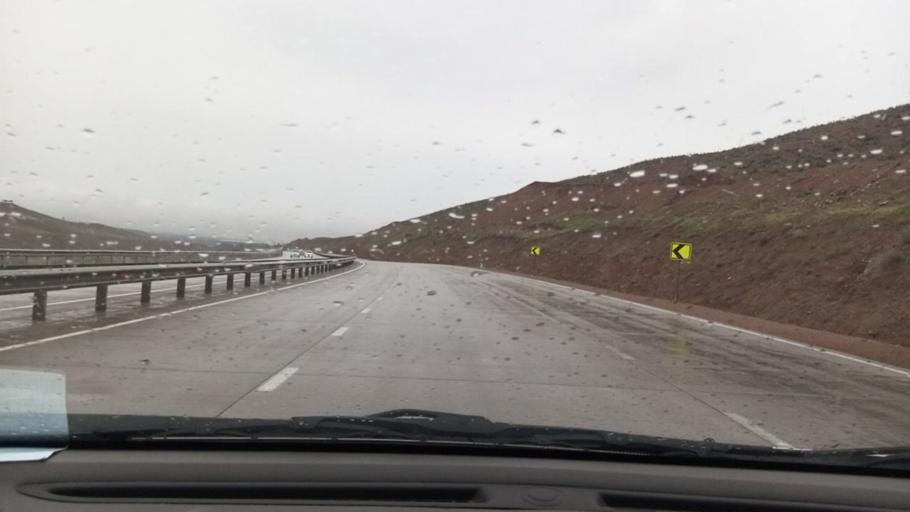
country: UZ
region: Namangan
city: Pop Shahri
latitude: 40.9314
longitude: 70.7031
